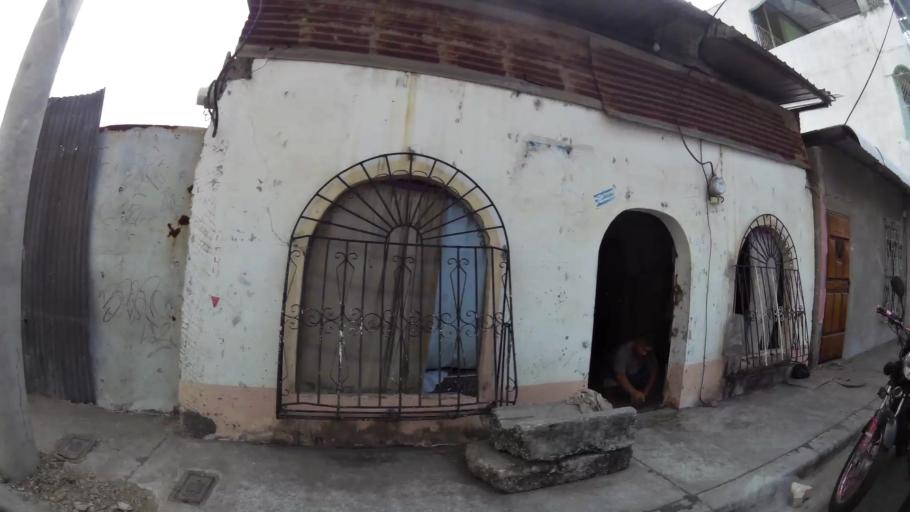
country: EC
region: Guayas
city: Guayaquil
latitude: -2.2598
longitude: -79.9018
